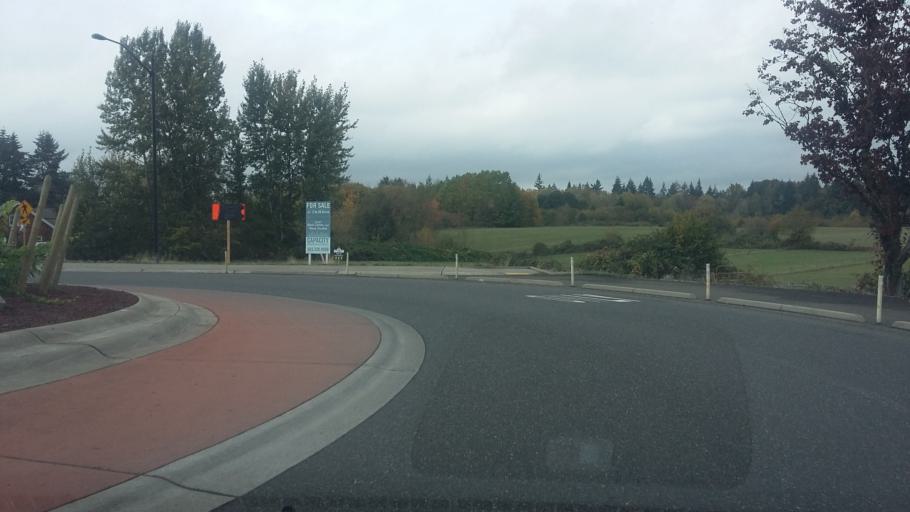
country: US
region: Washington
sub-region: Clark County
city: La Center
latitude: 45.8159
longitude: -122.6904
